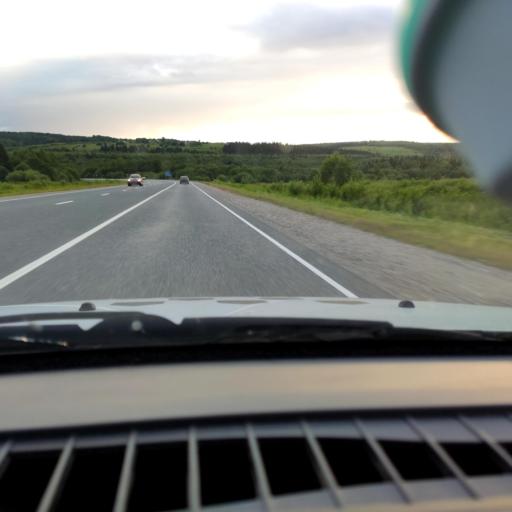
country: RU
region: Perm
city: Kalino
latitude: 58.2687
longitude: 57.3542
